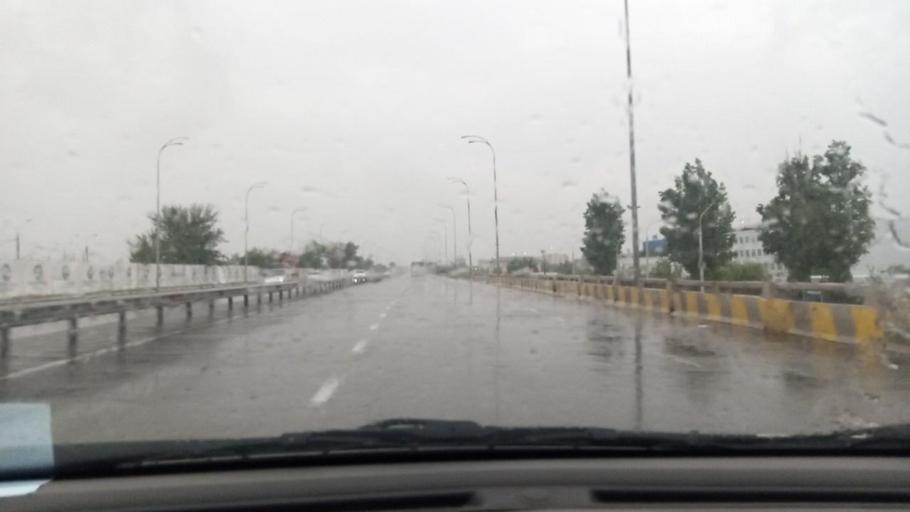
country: UZ
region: Toshkent Shahri
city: Bektemir
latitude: 41.2645
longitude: 69.3706
